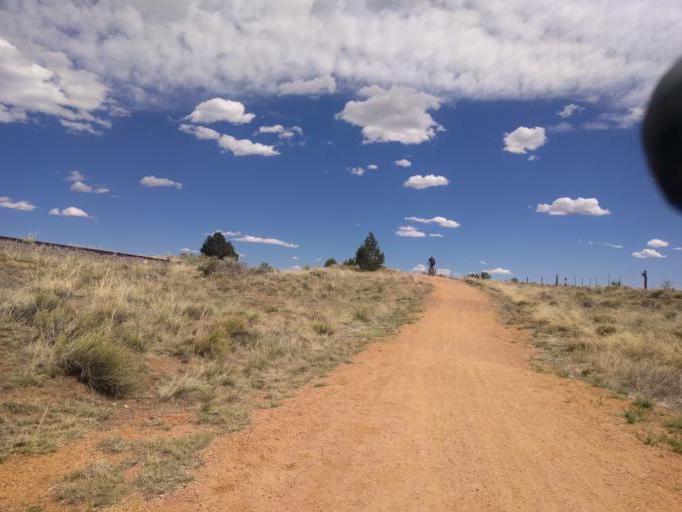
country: US
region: New Mexico
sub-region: Santa Fe County
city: Agua Fria
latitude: 35.6142
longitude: -105.9638
